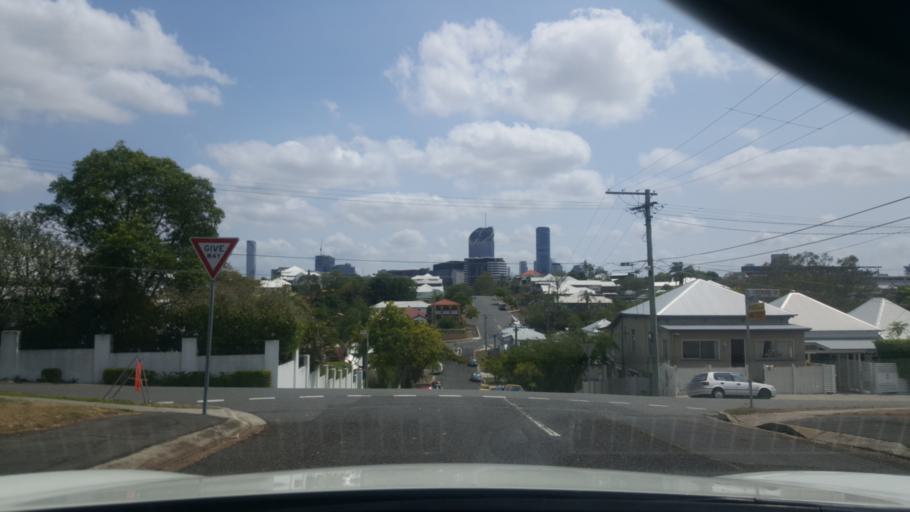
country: AU
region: Queensland
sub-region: Brisbane
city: South Brisbane
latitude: -27.4897
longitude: 153.0218
